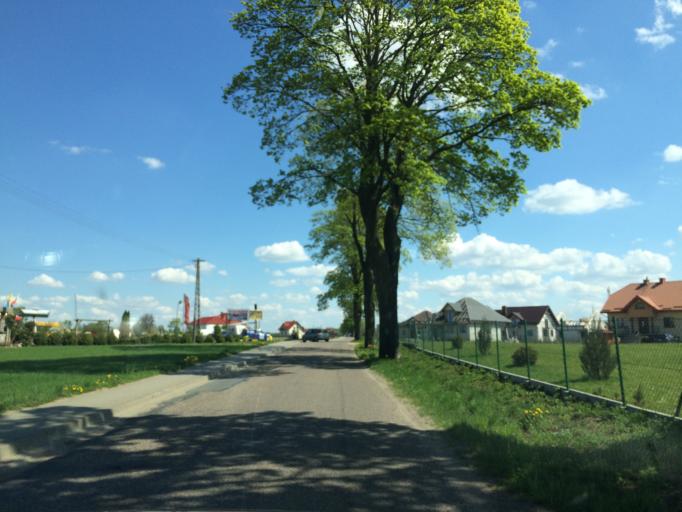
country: PL
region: Warmian-Masurian Voivodeship
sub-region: Powiat ilawski
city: Lubawa
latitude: 53.4121
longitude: 19.7685
